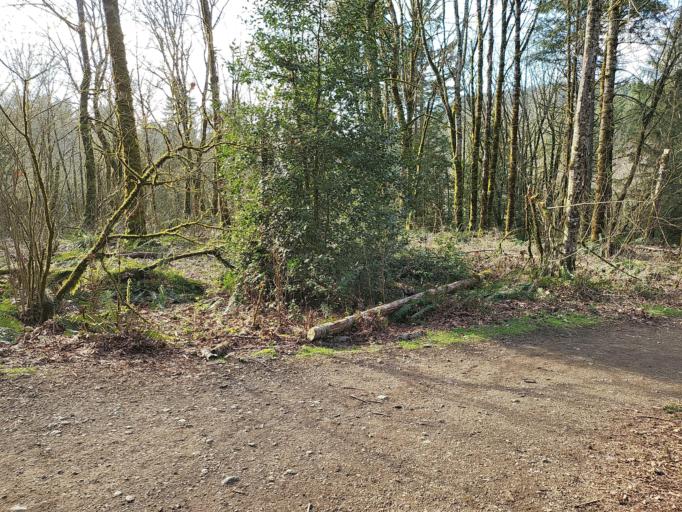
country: US
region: Washington
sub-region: King County
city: Newcastle
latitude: 47.5191
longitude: -122.1282
